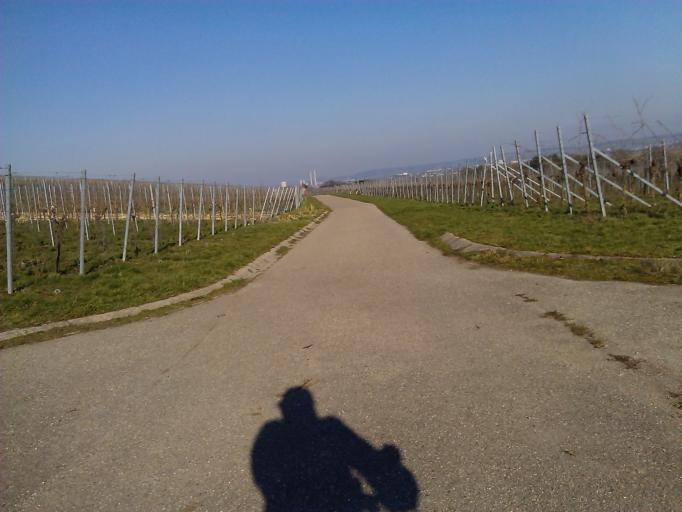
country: DE
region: Baden-Wuerttemberg
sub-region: Regierungsbezirk Stuttgart
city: Leingarten
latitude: 49.1256
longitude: 9.1099
